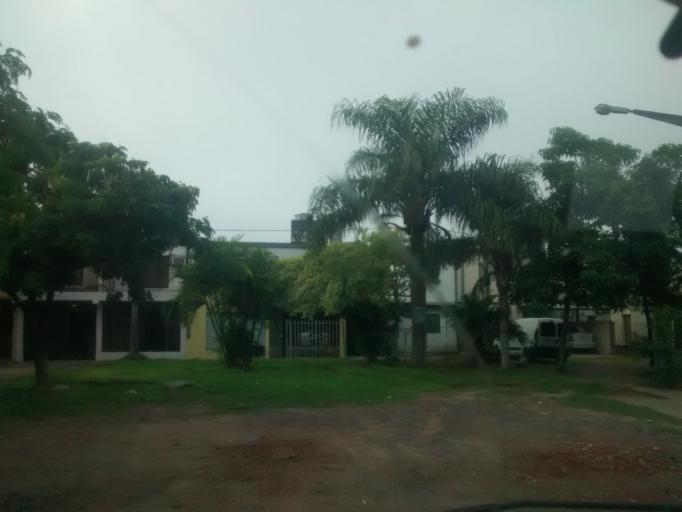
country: AR
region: Chaco
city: Resistencia
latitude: -27.4689
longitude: -58.9838
